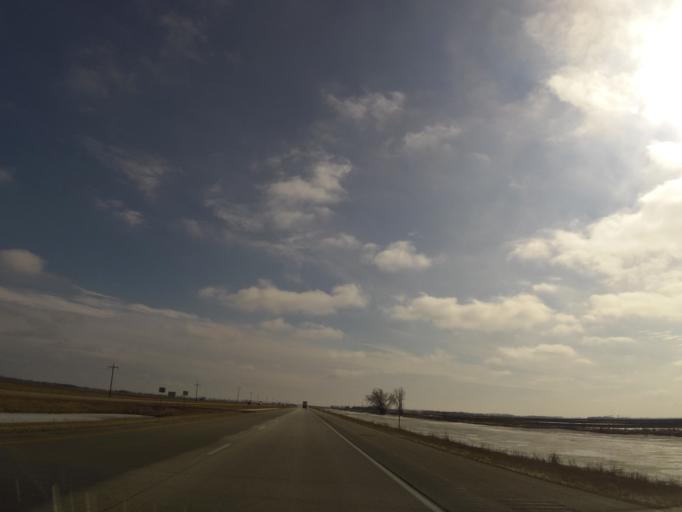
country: US
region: North Dakota
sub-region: Walsh County
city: Grafton
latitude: 48.3432
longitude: -97.1898
